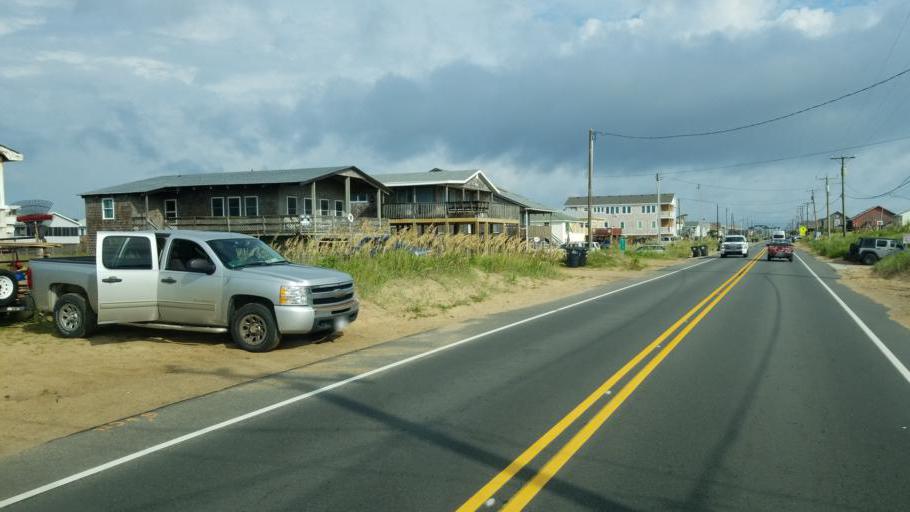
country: US
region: North Carolina
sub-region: Dare County
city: Kitty Hawk
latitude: 36.0886
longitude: -75.7041
